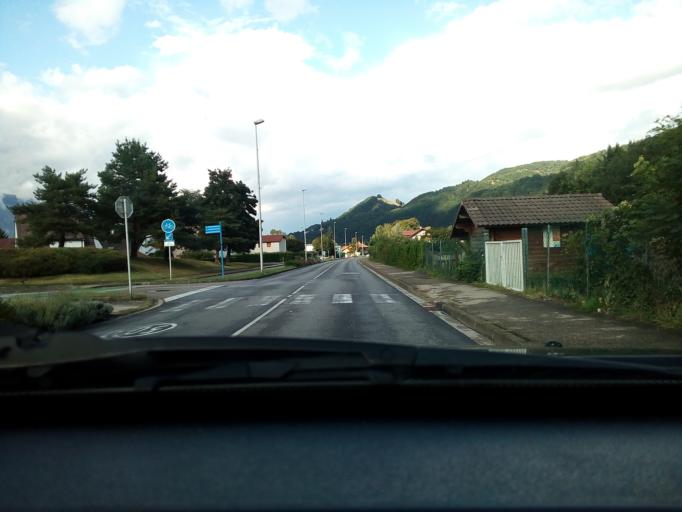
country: FR
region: Rhone-Alpes
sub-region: Departement de l'Isere
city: Eybens
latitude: 45.1548
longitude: 5.7528
